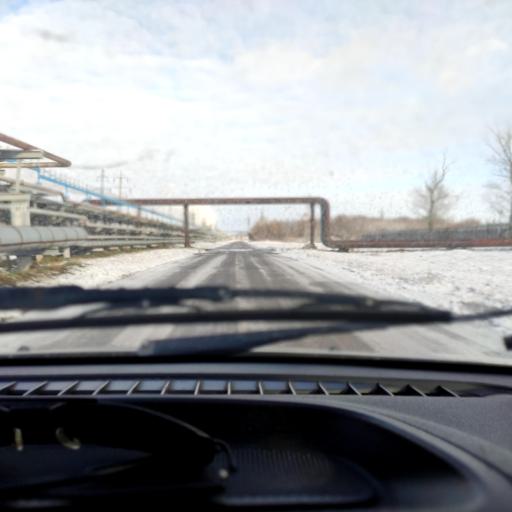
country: RU
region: Samara
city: Zhigulevsk
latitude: 53.5347
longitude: 49.4819
